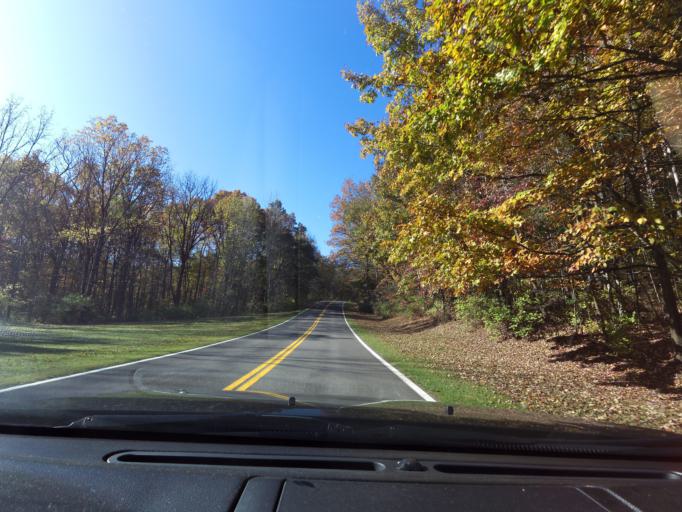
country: US
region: New York
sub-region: Wyoming County
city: Castile
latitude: 42.6392
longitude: -77.9863
